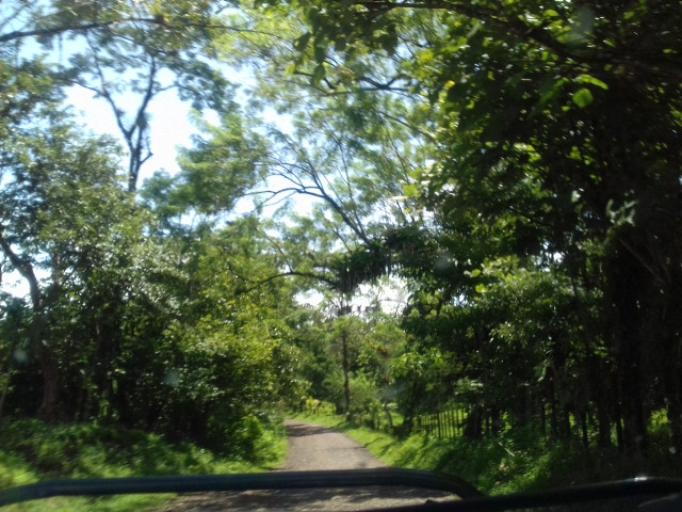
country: NI
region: Matagalpa
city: Rio Blanco
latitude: 12.9772
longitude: -85.3642
